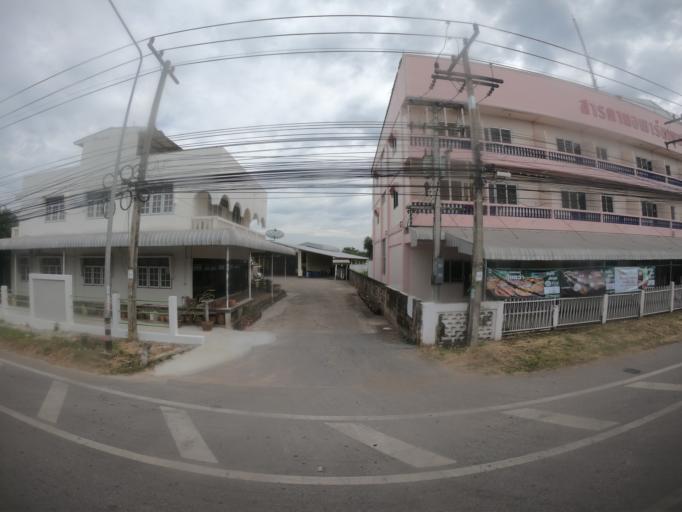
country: TH
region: Maha Sarakham
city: Maha Sarakham
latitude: 16.1992
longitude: 103.2930
